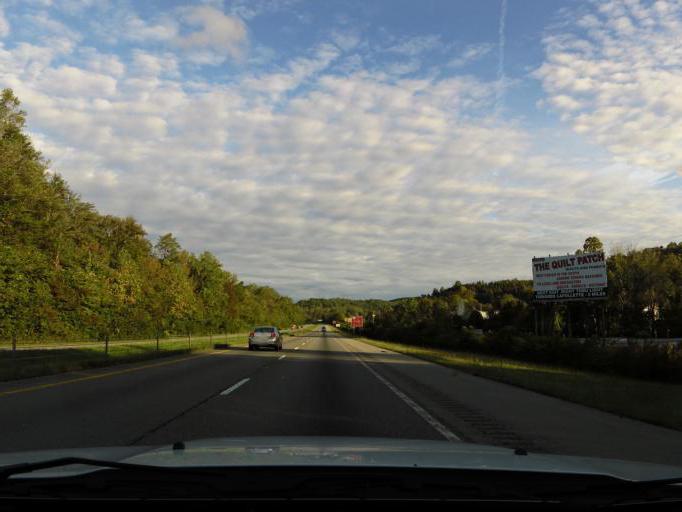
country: US
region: Tennessee
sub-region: Anderson County
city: Rocky Top
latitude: 36.2537
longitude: -84.1839
